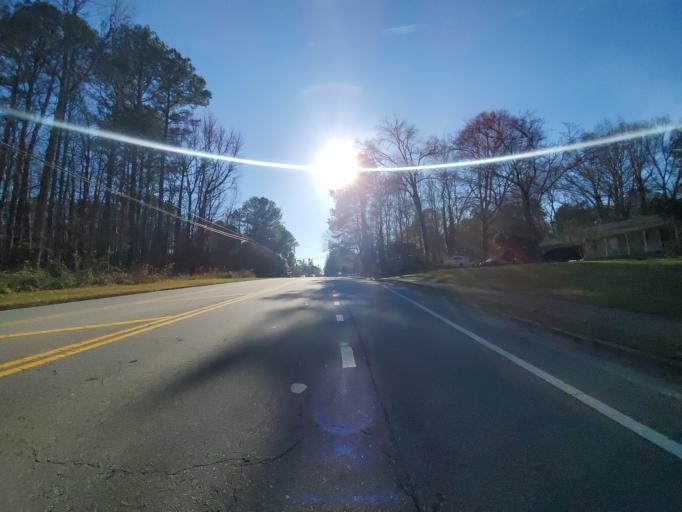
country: US
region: Georgia
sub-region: Gwinnett County
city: Lilburn
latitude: 33.8880
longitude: -84.0911
